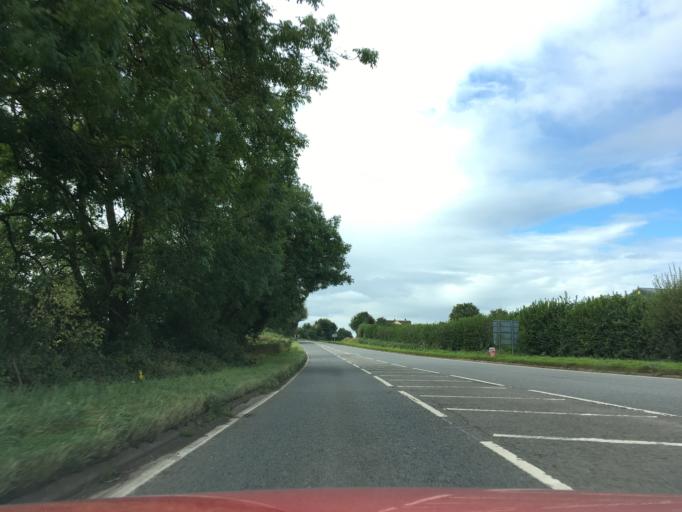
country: GB
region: England
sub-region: Gloucestershire
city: Bream
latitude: 51.6894
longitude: -2.5970
